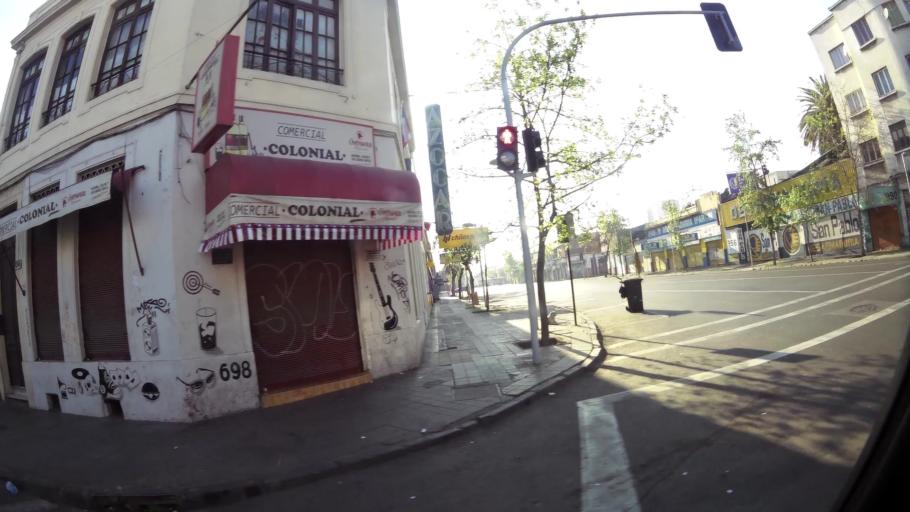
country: CL
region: Santiago Metropolitan
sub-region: Provincia de Santiago
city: Santiago
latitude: -33.4539
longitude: -70.6483
